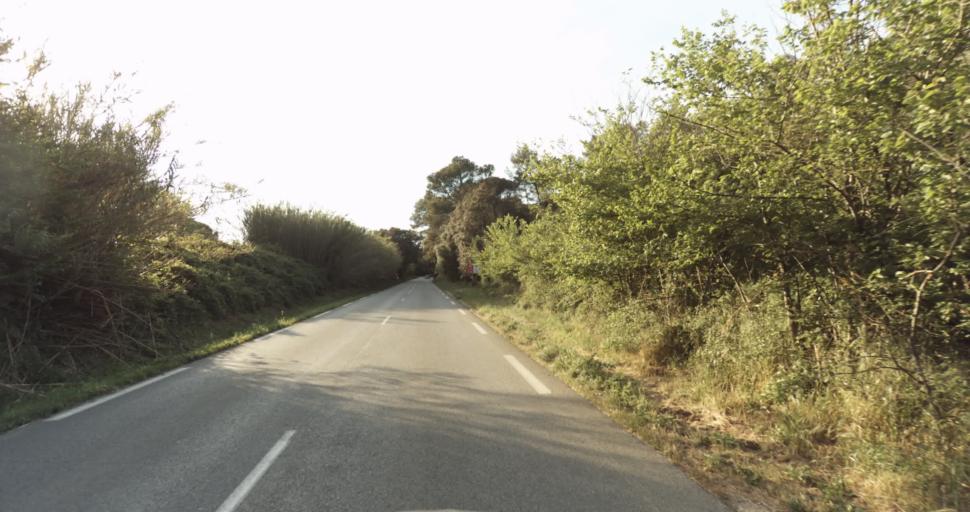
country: FR
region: Provence-Alpes-Cote d'Azur
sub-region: Departement du Var
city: Hyeres
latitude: 43.1630
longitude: 6.1222
